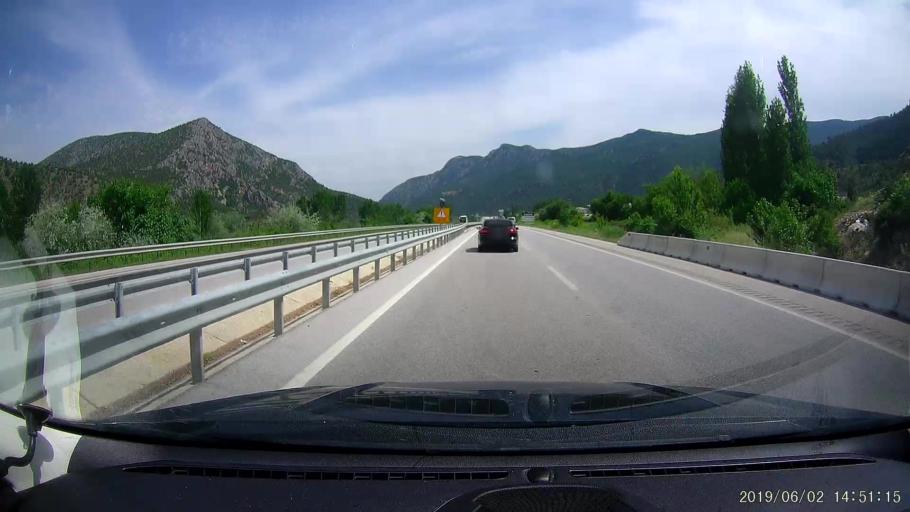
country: TR
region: Corum
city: Kargi
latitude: 41.0631
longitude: 34.5374
